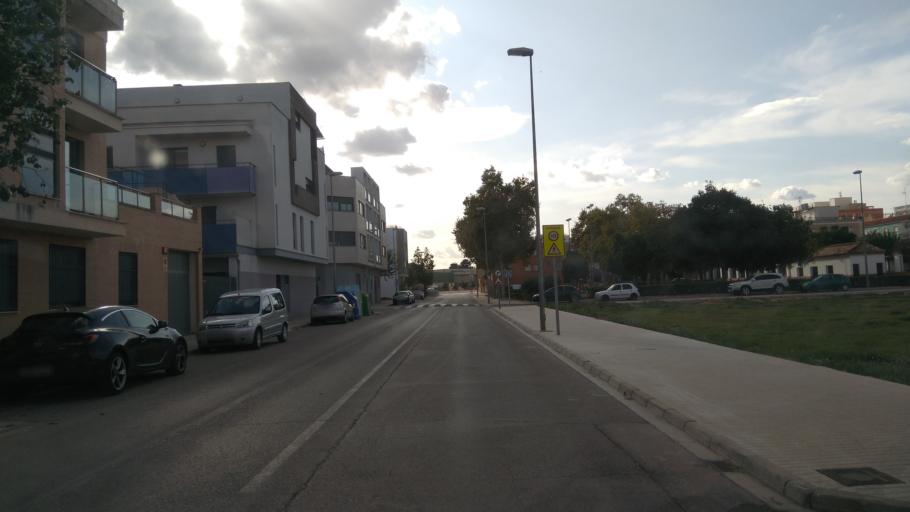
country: ES
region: Valencia
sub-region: Provincia de Valencia
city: L'Alcudia
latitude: 39.1918
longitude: -0.5032
